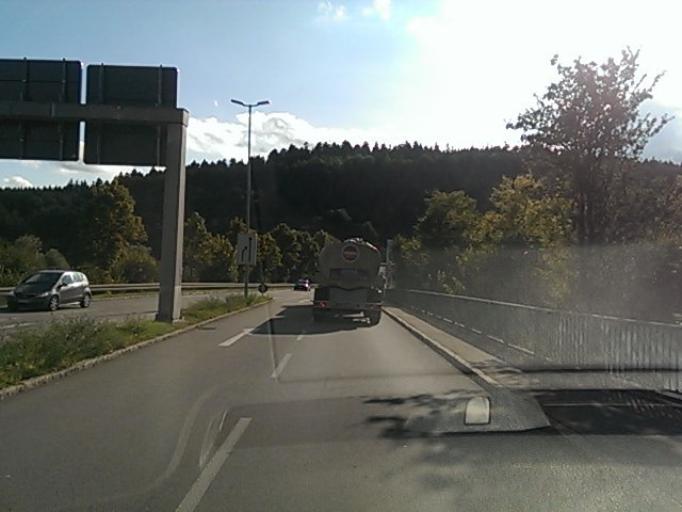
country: DE
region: Baden-Wuerttemberg
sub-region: Freiburg Region
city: Wurmlingen
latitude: 47.9889
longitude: 8.7986
